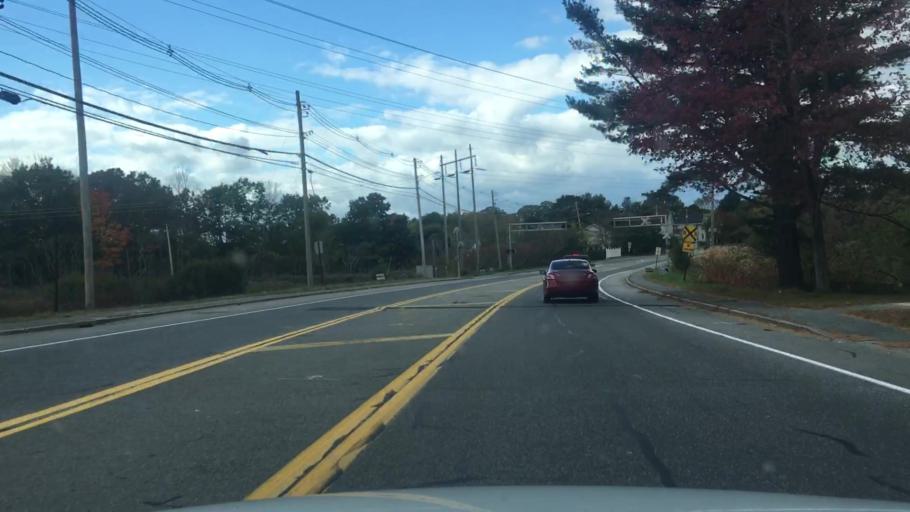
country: US
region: Maine
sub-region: Cumberland County
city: South Portland Gardens
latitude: 43.6585
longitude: -70.3002
